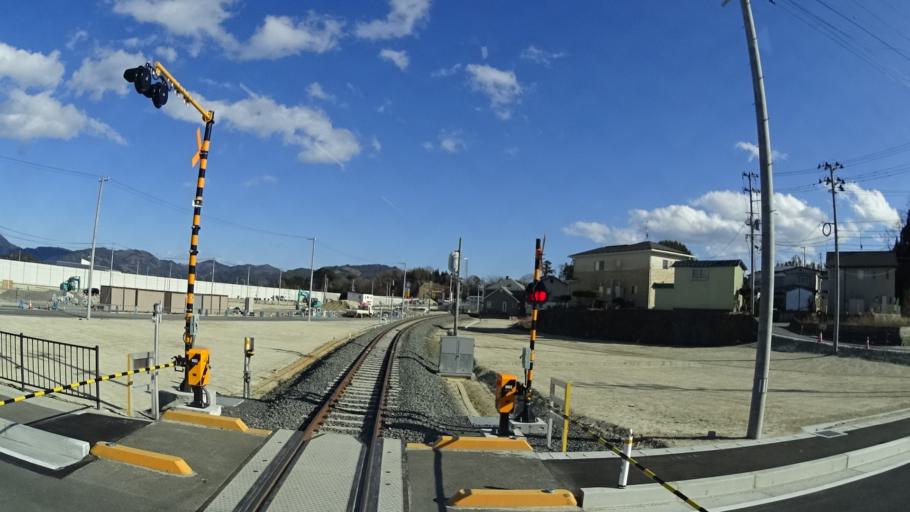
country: JP
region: Iwate
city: Yamada
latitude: 39.4622
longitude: 141.9532
